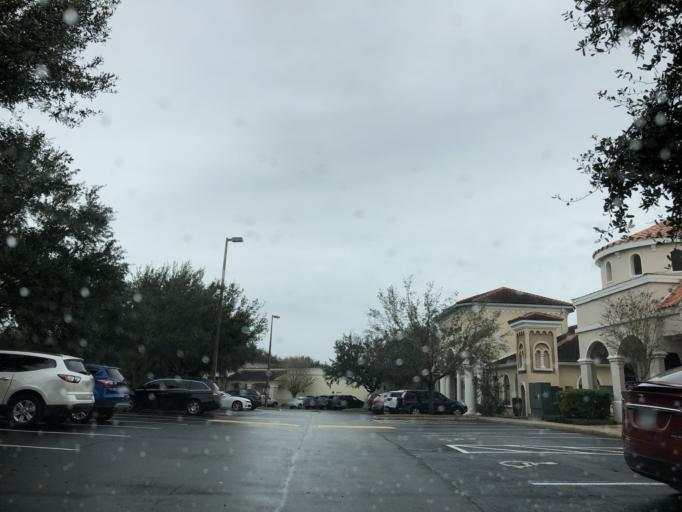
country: US
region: Florida
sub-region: Orange County
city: Doctor Phillips
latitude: 28.4288
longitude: -81.4812
